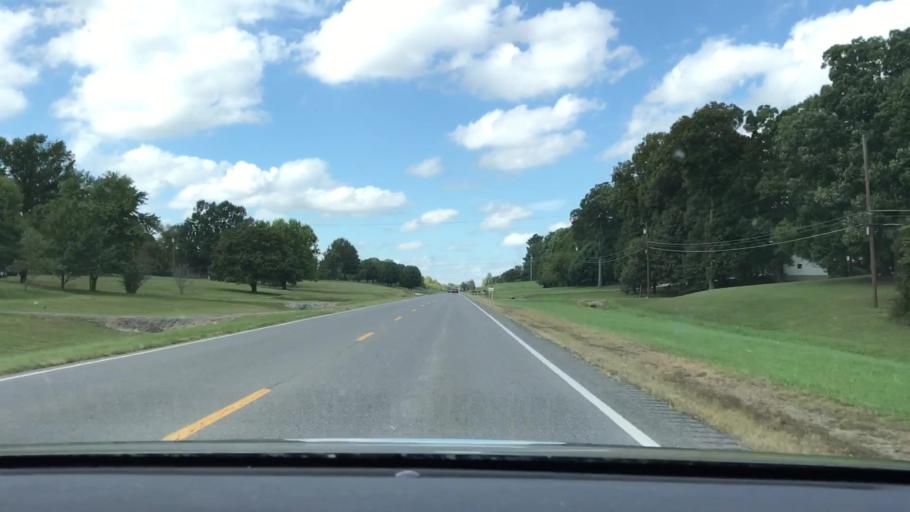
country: US
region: Kentucky
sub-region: Livingston County
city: Ledbetter
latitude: 37.0077
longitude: -88.4857
